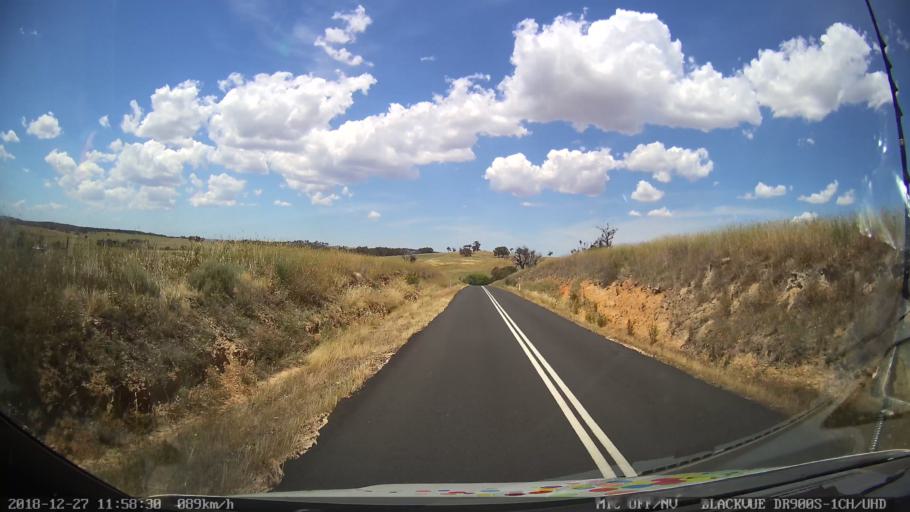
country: AU
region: New South Wales
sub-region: Blayney
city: Blayney
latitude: -33.7246
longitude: 149.3835
